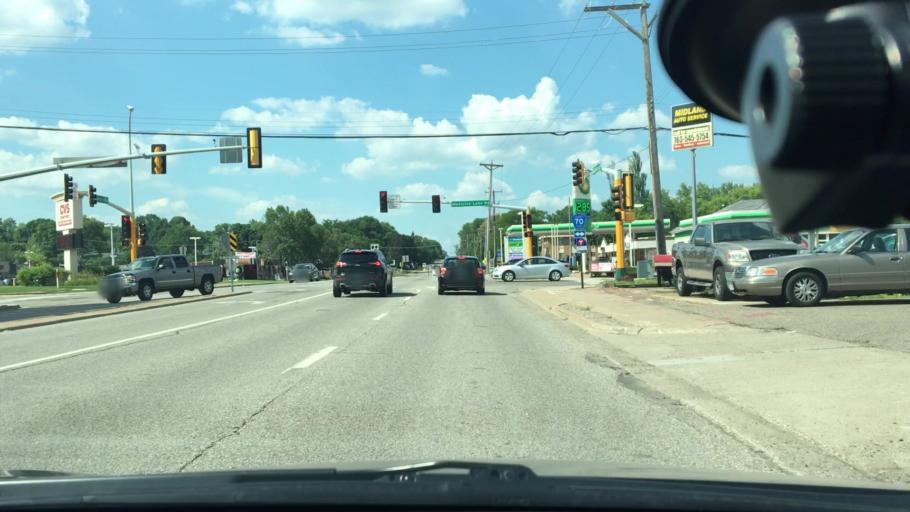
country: US
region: Minnesota
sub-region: Hennepin County
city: Golden Valley
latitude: 45.0069
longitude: -93.3802
